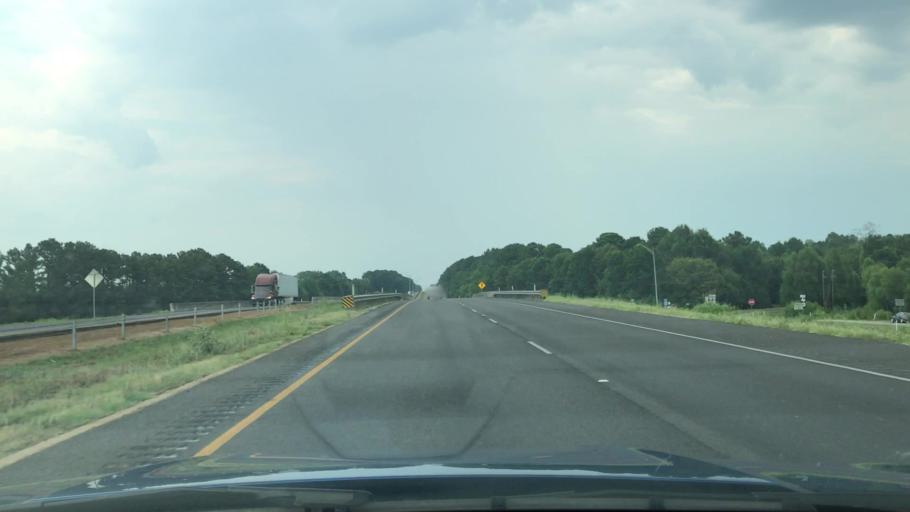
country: US
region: Texas
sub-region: Harrison County
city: Marshall
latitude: 32.4935
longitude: -94.2981
